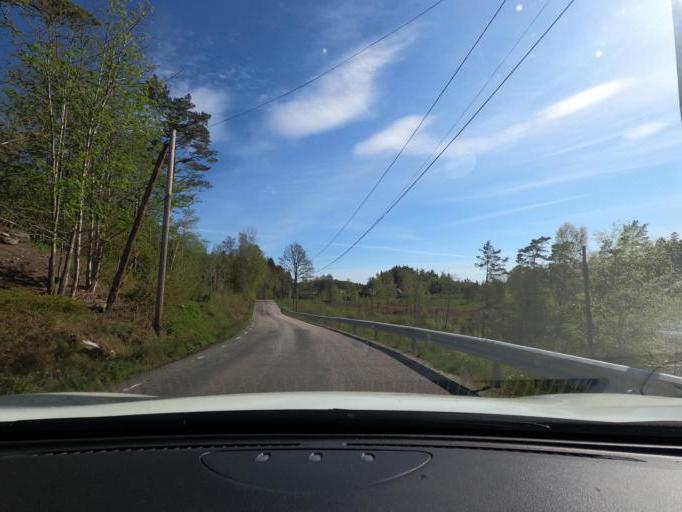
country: SE
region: Vaestra Goetaland
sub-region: Harryda Kommun
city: Hindas
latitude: 57.6432
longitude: 12.3518
